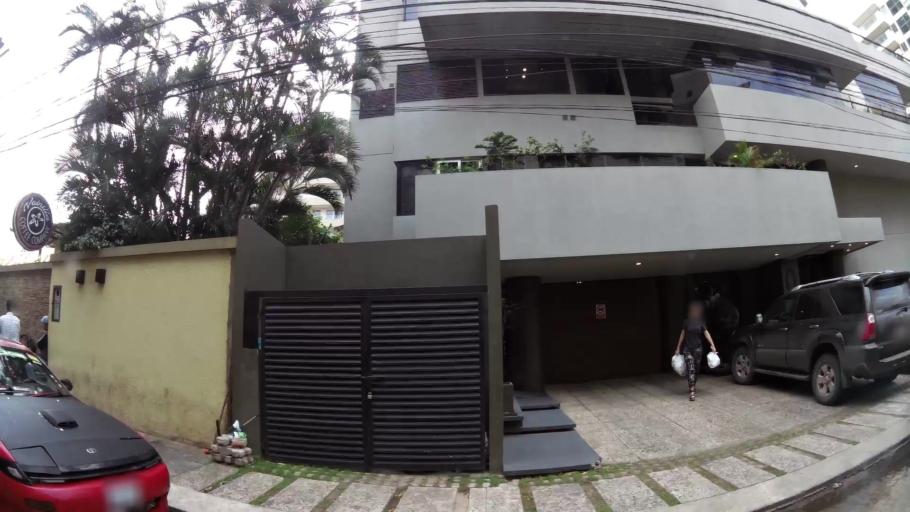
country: BO
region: Santa Cruz
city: Santa Cruz de la Sierra
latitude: -17.7714
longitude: -63.1918
